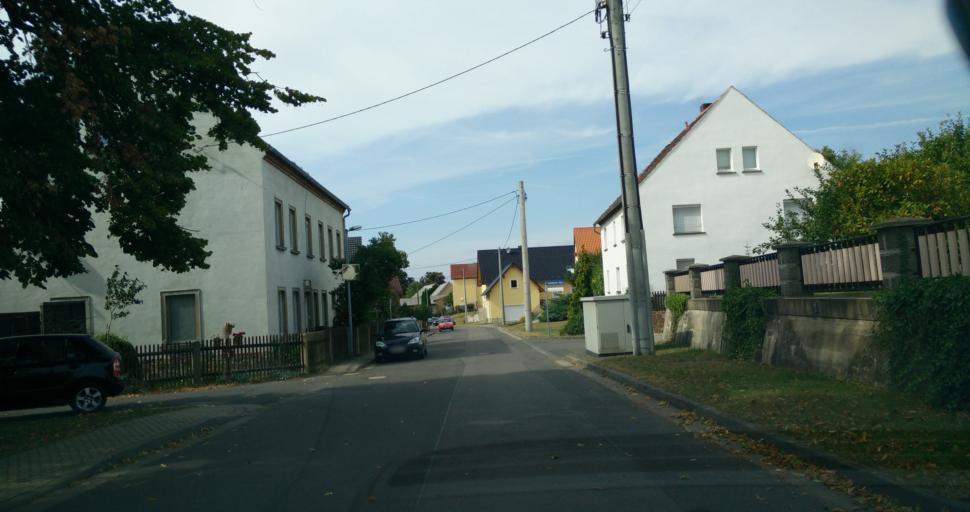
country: DE
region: Saxony
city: Bad Lausick
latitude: 51.1344
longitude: 12.6972
